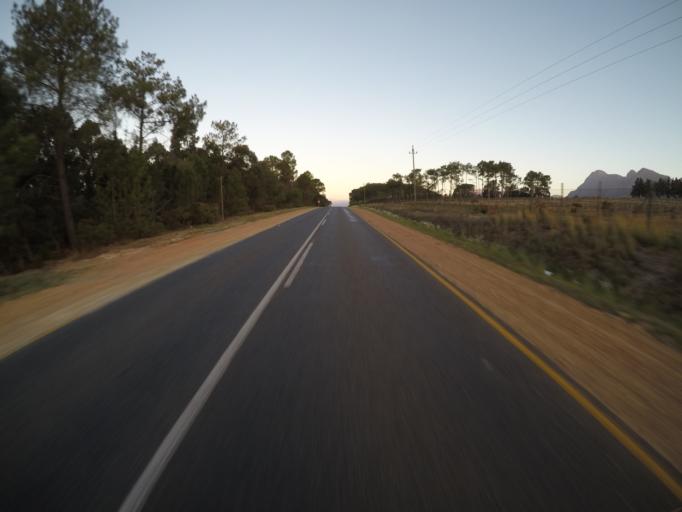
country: ZA
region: Western Cape
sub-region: Cape Winelands District Municipality
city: Paarl
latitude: -33.8118
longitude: 18.9097
